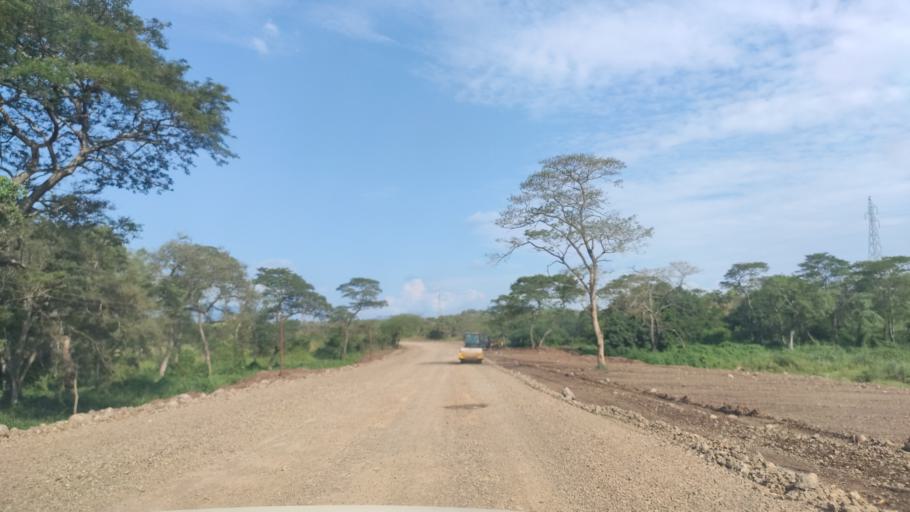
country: ET
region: Southern Nations, Nationalities, and People's Region
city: Felege Neway
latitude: 6.4283
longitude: 37.2060
